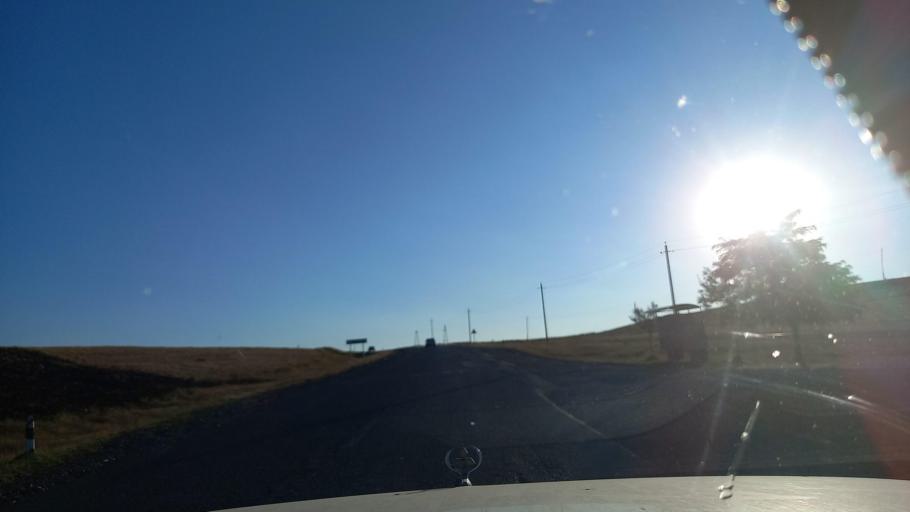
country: AZ
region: Shamkir Rayon
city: Shamkhor
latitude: 40.7589
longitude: 45.9084
